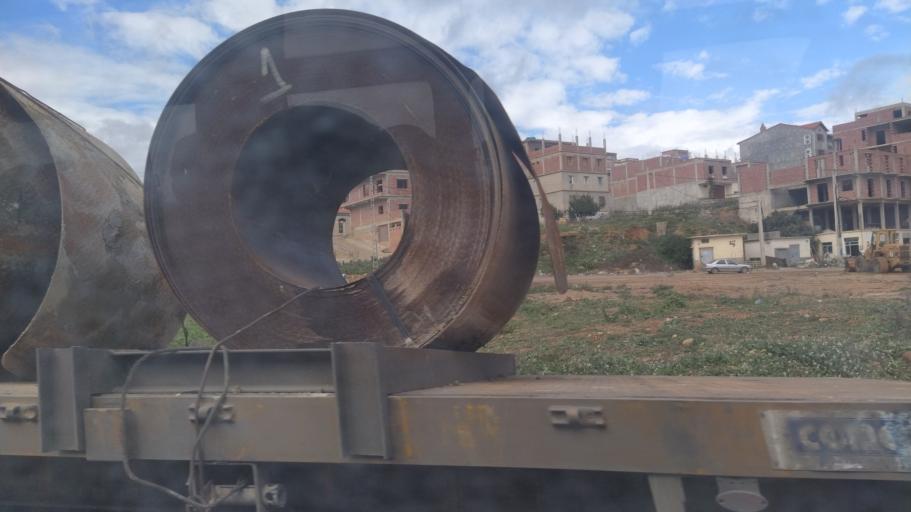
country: DZ
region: Constantine
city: El Khroub
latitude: 36.3051
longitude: 6.6850
